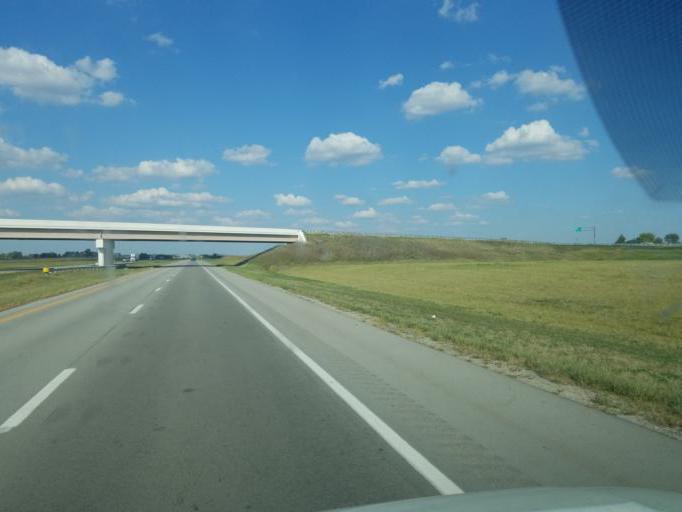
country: US
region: Ohio
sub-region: Wyandot County
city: Upper Sandusky
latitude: 40.8317
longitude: -83.3364
